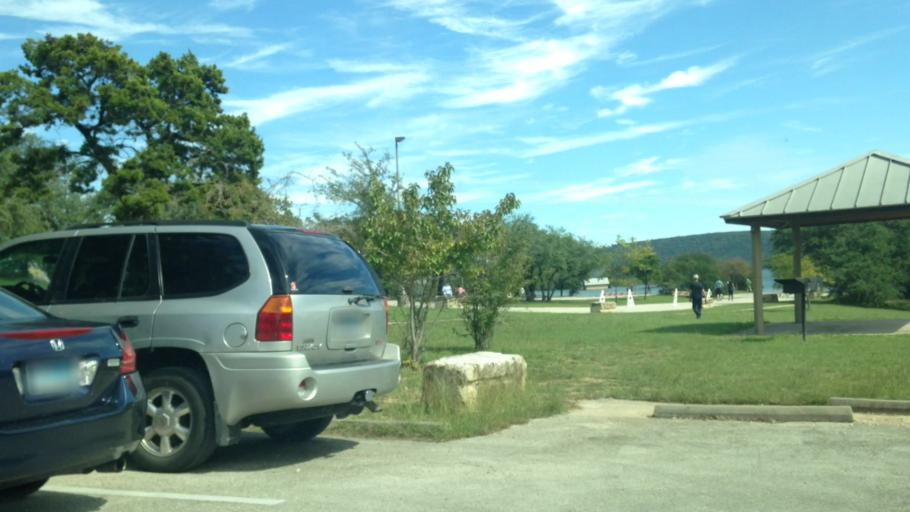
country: US
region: Texas
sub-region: Travis County
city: Hudson Bend
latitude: 30.3952
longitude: -97.9070
